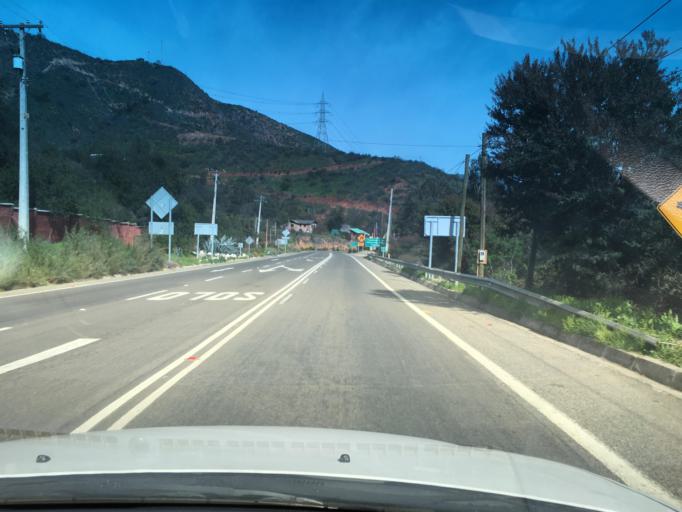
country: CL
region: Valparaiso
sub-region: Provincia de Marga Marga
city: Limache
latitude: -33.0596
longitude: -71.0523
